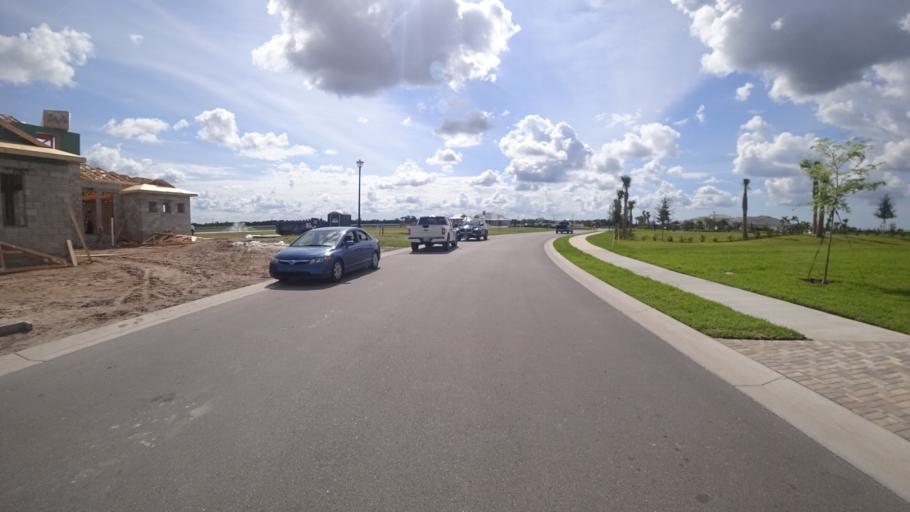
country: US
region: Florida
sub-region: Sarasota County
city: The Meadows
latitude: 27.3910
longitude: -82.3606
